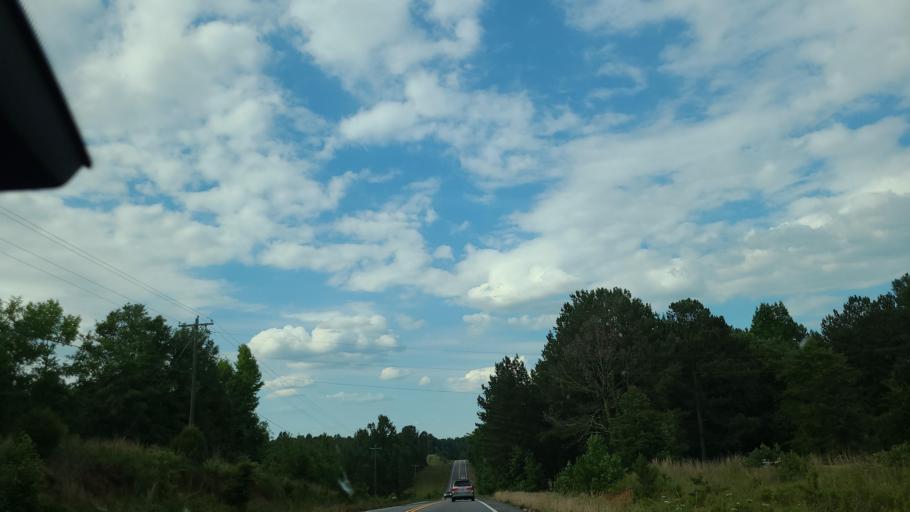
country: US
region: Georgia
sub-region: Putnam County
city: Eatonton
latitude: 33.2478
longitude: -83.4297
